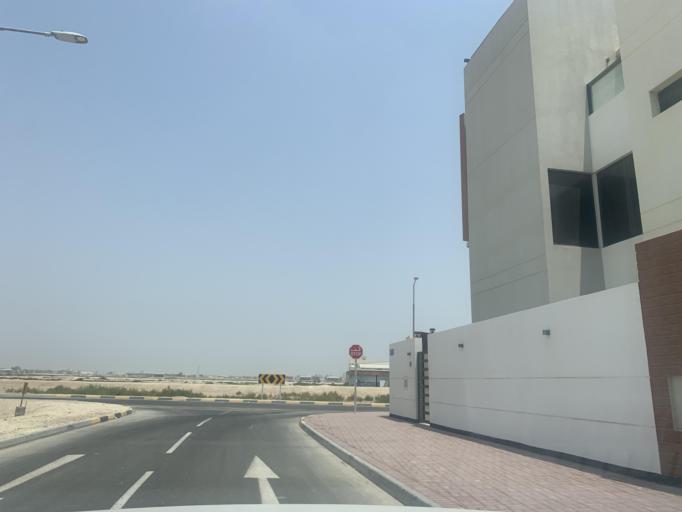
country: BH
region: Central Governorate
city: Madinat Hamad
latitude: 26.1336
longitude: 50.4696
